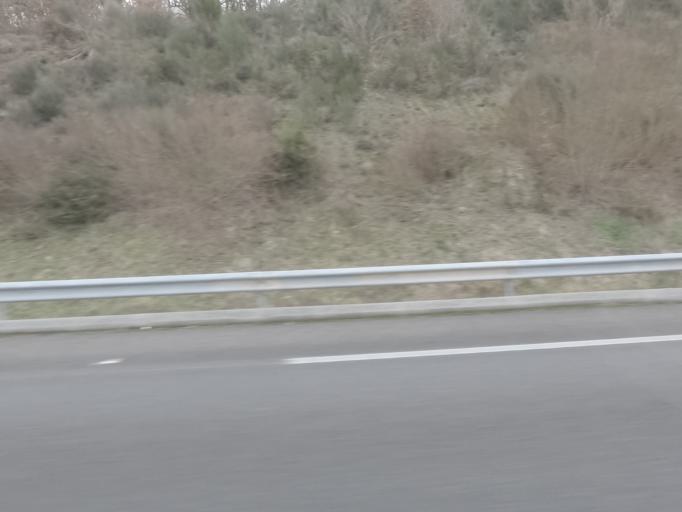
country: ES
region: Galicia
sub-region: Provincia de Ourense
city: Punxin
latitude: 42.3765
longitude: -7.9919
